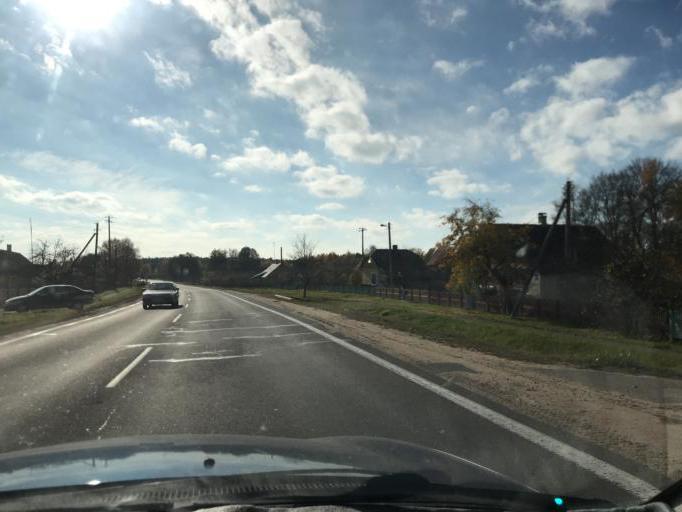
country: LT
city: Salcininkai
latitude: 54.2411
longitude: 25.3548
